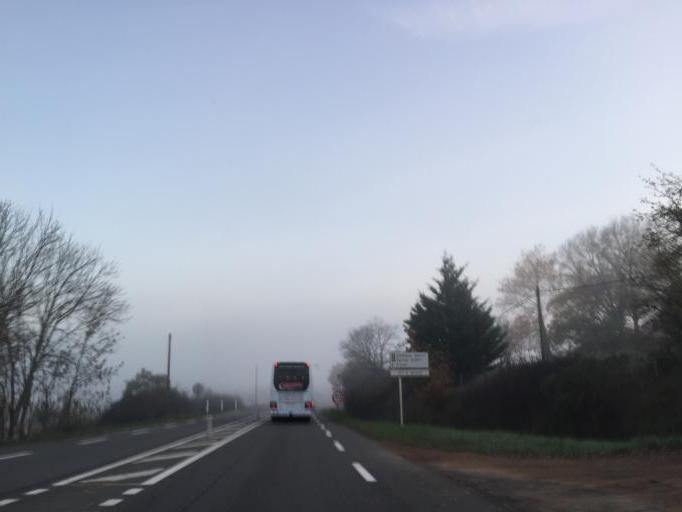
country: FR
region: Rhone-Alpes
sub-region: Departement de la Loire
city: Balbigny
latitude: 45.8570
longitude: 4.1726
